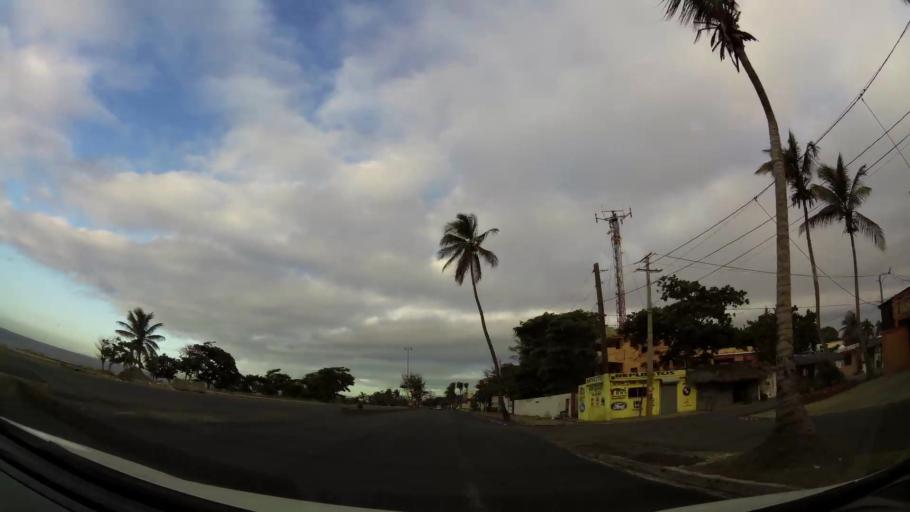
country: DO
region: Nacional
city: Bella Vista
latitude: 18.4269
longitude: -69.9755
